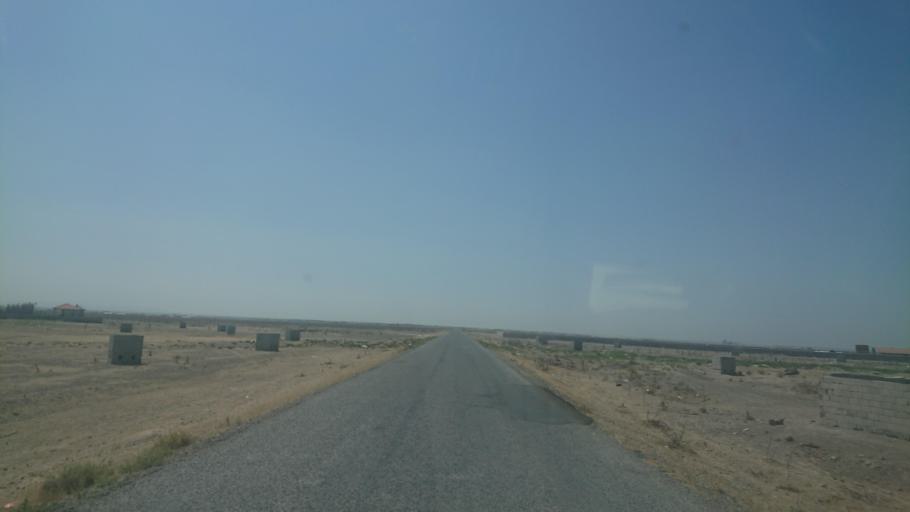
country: TR
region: Aksaray
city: Yesilova
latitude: 38.3276
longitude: 33.7475
